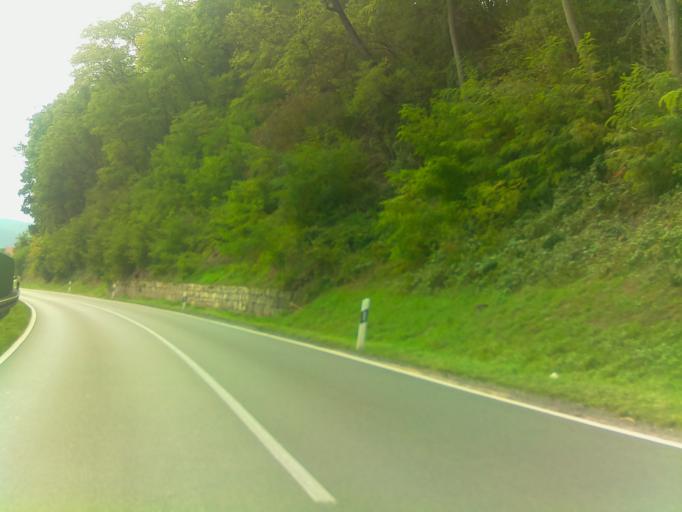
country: DE
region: Thuringia
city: Grosseutersdorf
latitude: 50.7933
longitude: 11.5681
